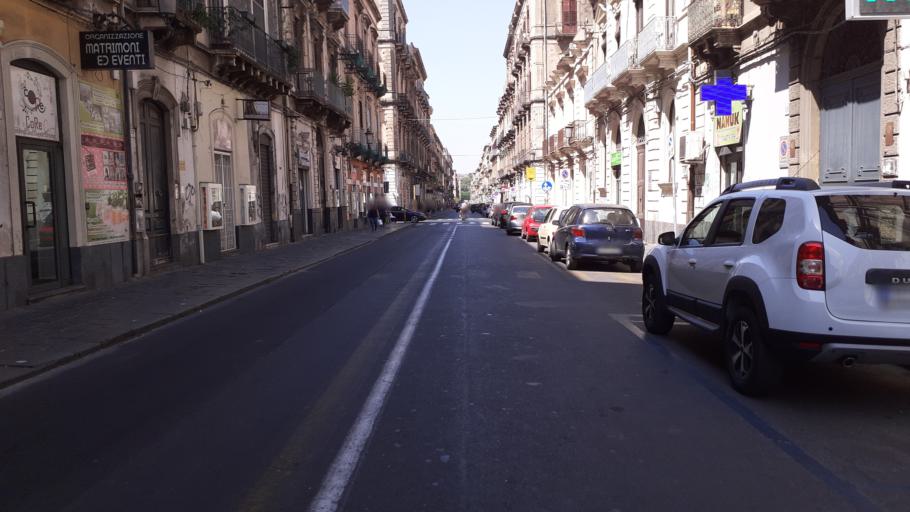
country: IT
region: Sicily
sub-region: Catania
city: Canalicchio
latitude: 37.5124
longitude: 15.0947
